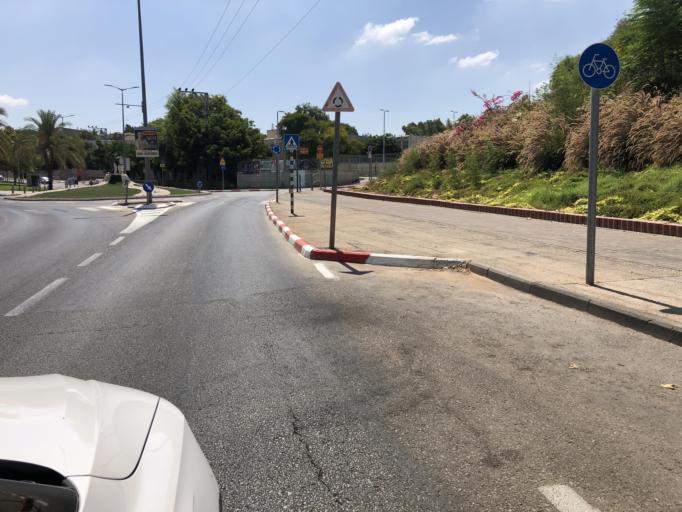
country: IL
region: Central District
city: Rosh Ha'Ayin
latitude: 32.0982
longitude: 34.9582
